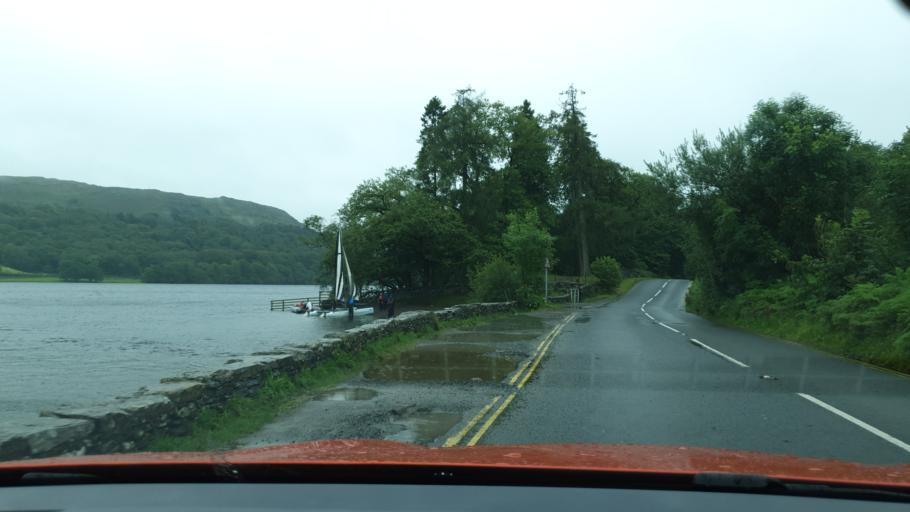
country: GB
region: England
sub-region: Cumbria
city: Ulverston
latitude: 54.3124
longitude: -3.0917
